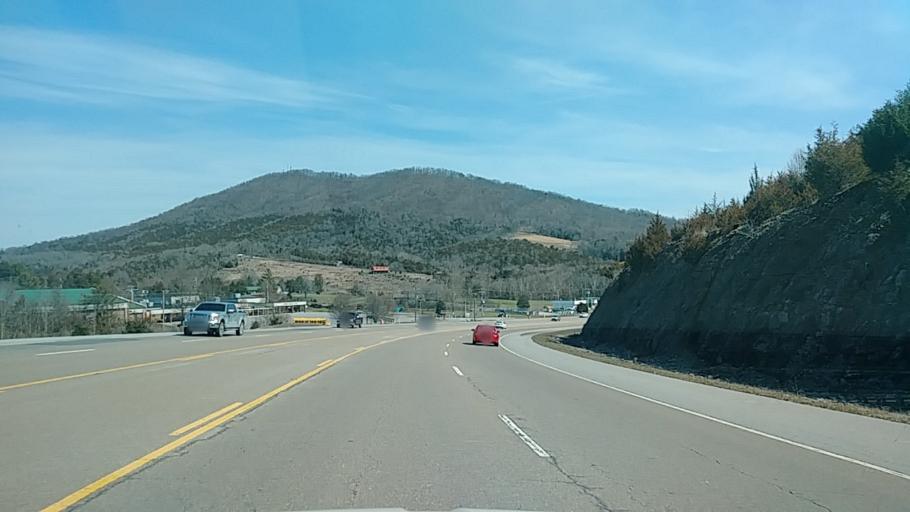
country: US
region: Tennessee
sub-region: Claiborne County
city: Tazewell
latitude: 36.4239
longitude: -83.5290
